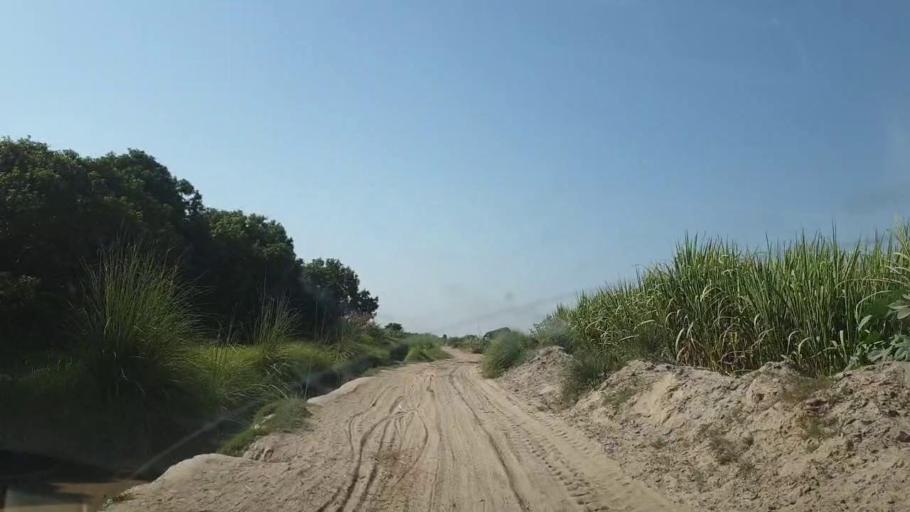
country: PK
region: Sindh
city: Tando Jam
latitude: 25.3168
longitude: 68.6044
